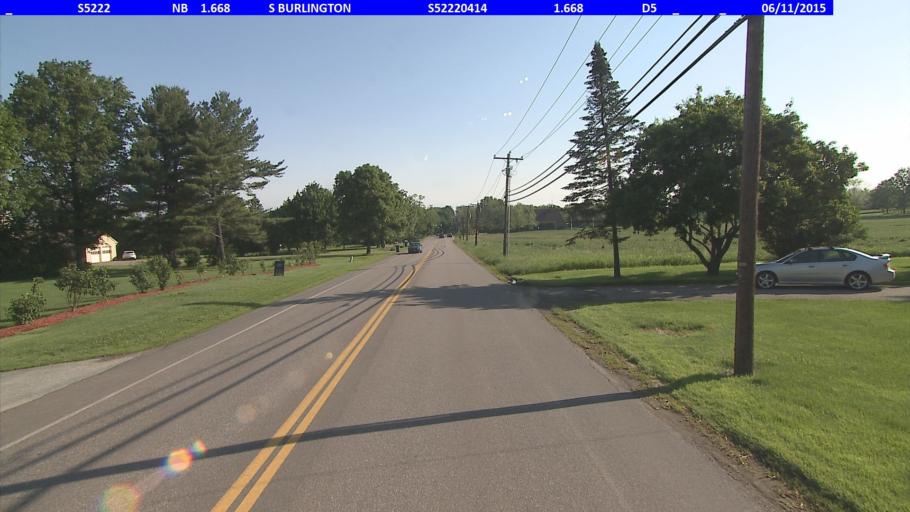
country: US
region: Vermont
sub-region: Chittenden County
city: South Burlington
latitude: 44.4406
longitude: -73.1898
